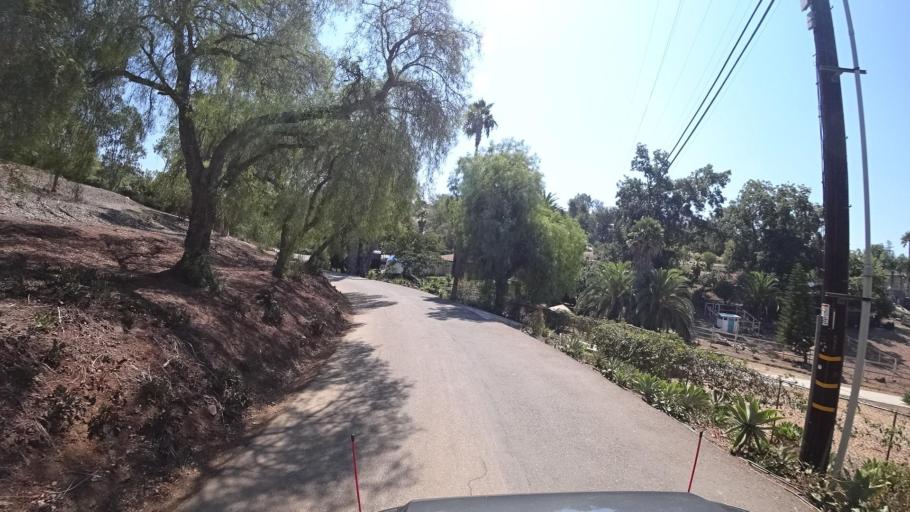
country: US
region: California
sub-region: San Diego County
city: San Marcos
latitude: 33.1733
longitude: -117.1984
